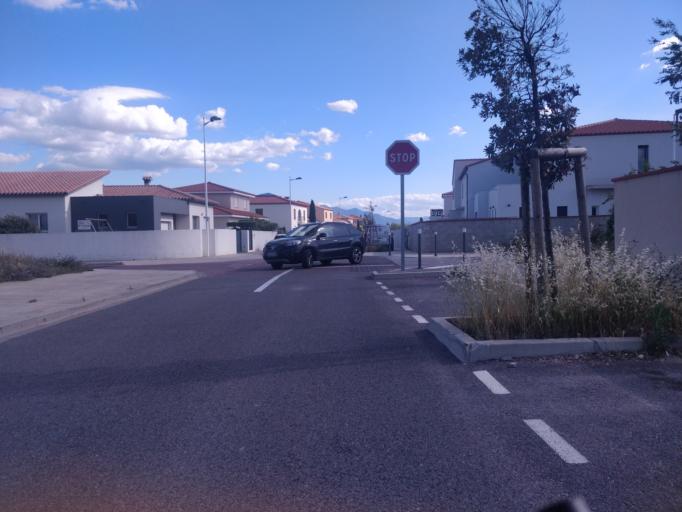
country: FR
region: Languedoc-Roussillon
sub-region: Departement des Pyrenees-Orientales
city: Saleilles
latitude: 42.6598
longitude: 2.9389
